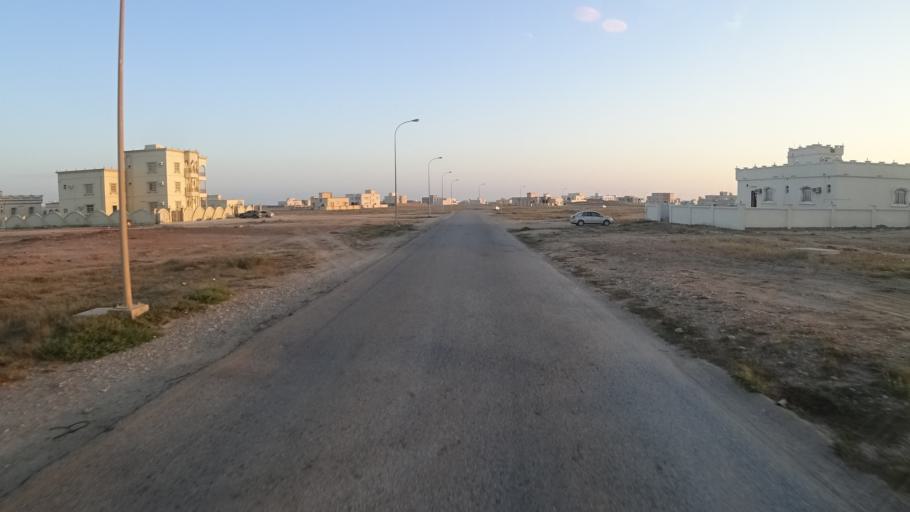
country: OM
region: Zufar
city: Salalah
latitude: 16.9958
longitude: 54.7195
